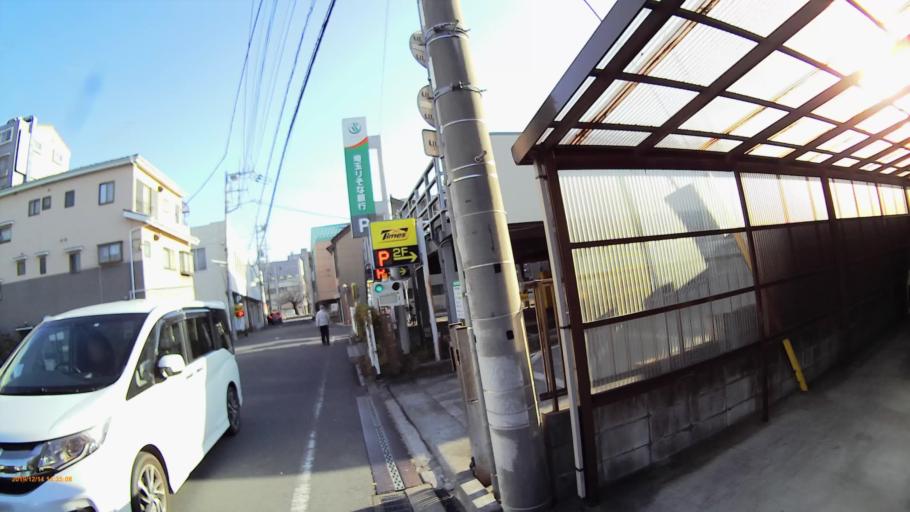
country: JP
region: Saitama
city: Konosu
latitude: 36.0329
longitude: 139.5339
